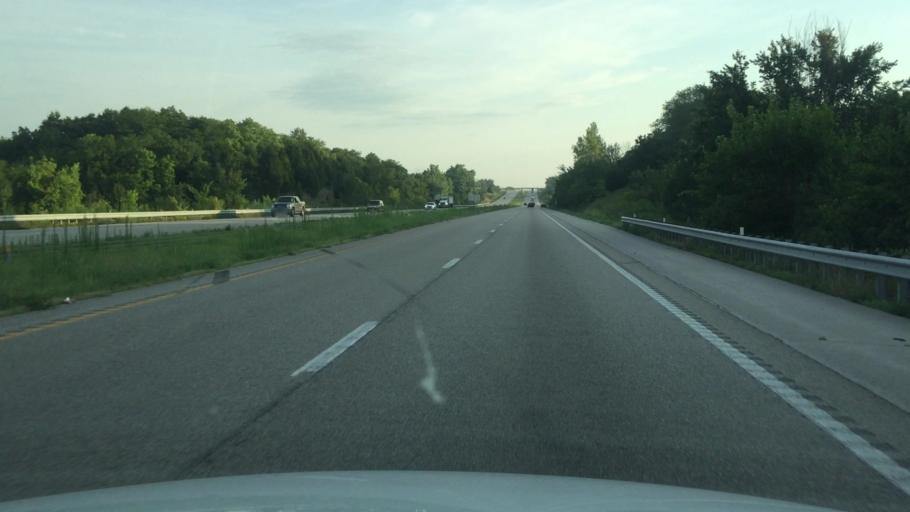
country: US
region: Missouri
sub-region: Platte County
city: Platte City
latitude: 39.4623
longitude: -94.7880
